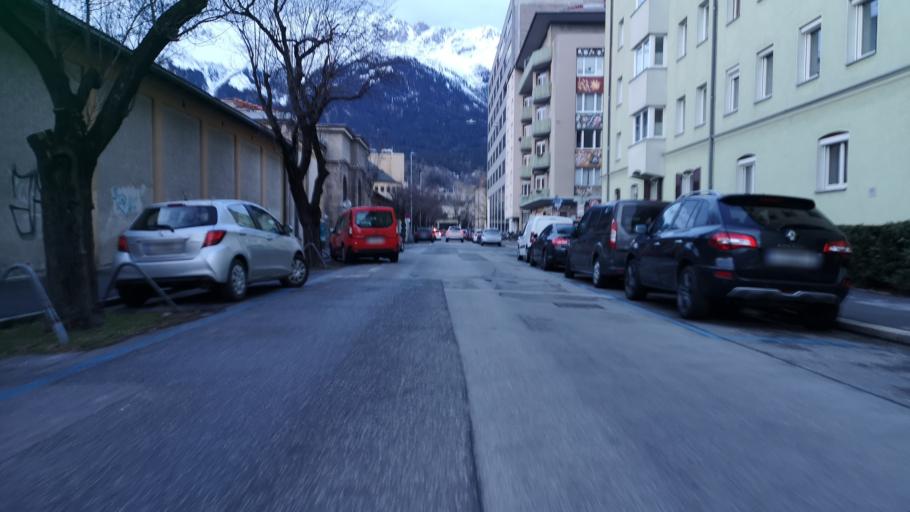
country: AT
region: Tyrol
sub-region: Innsbruck Stadt
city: Innsbruck
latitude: 47.2585
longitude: 11.3869
